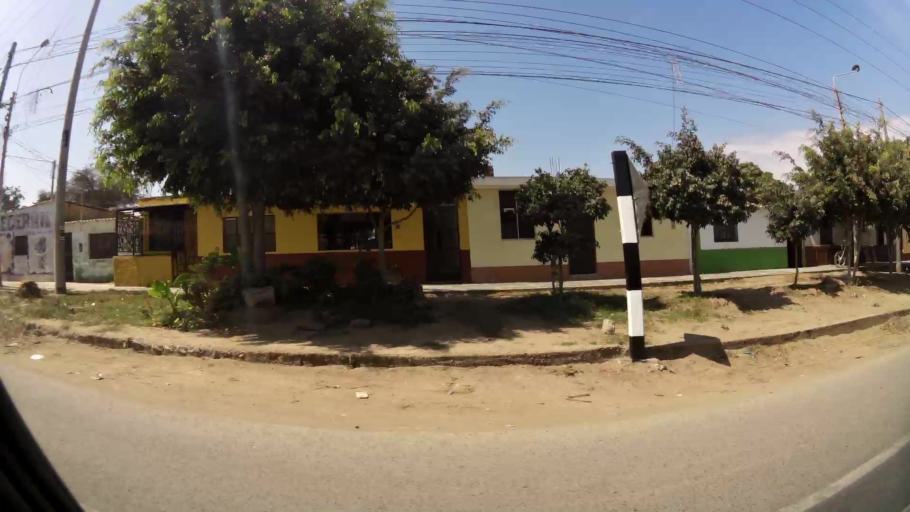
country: PE
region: Lambayeque
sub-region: Provincia de Chiclayo
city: Mocupe
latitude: -6.9881
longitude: -79.6269
